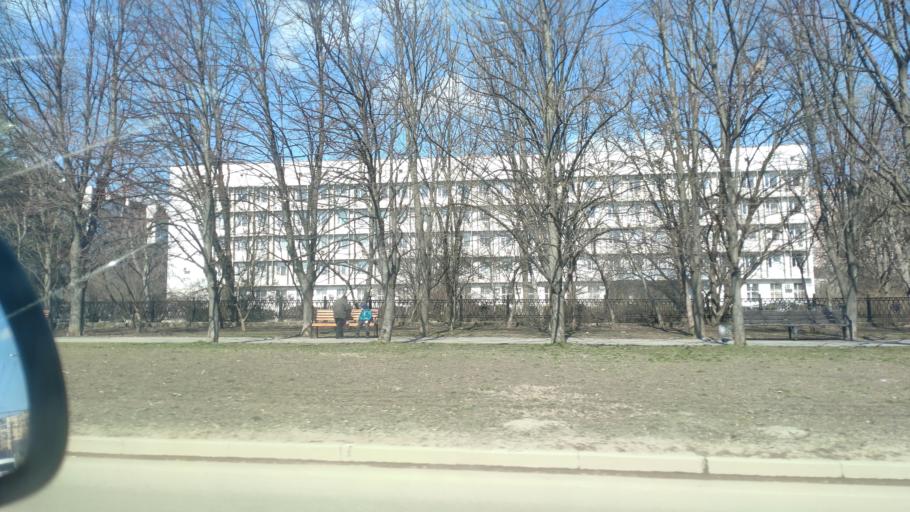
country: RU
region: Krasnodarskiy
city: Krasnodar
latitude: 45.0558
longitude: 39.0138
